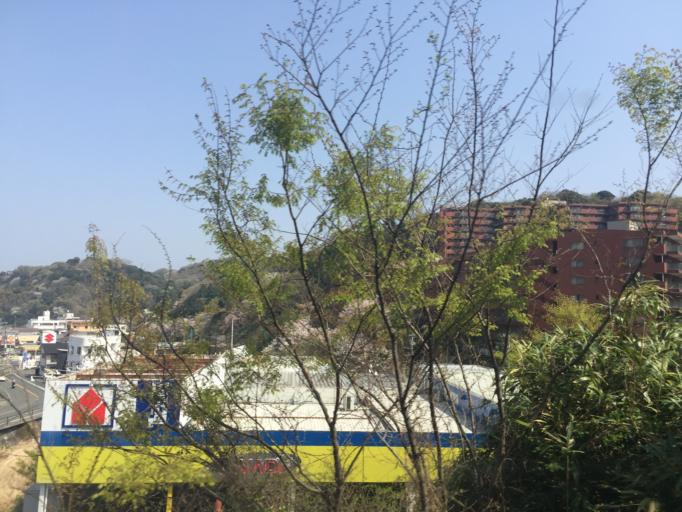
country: JP
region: Shizuoka
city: Ito
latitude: 34.9529
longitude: 139.0880
